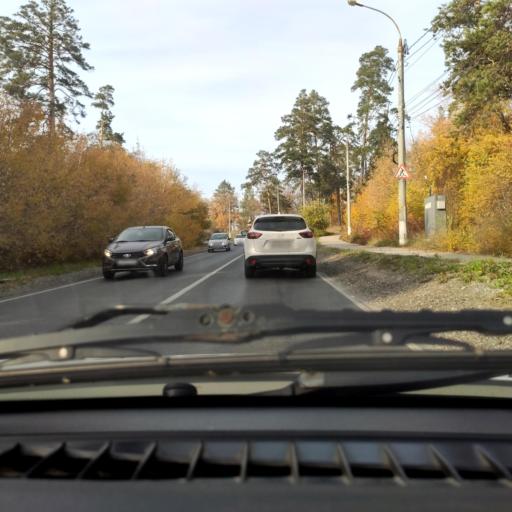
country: RU
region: Samara
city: Tol'yatti
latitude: 53.4799
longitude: 49.3226
